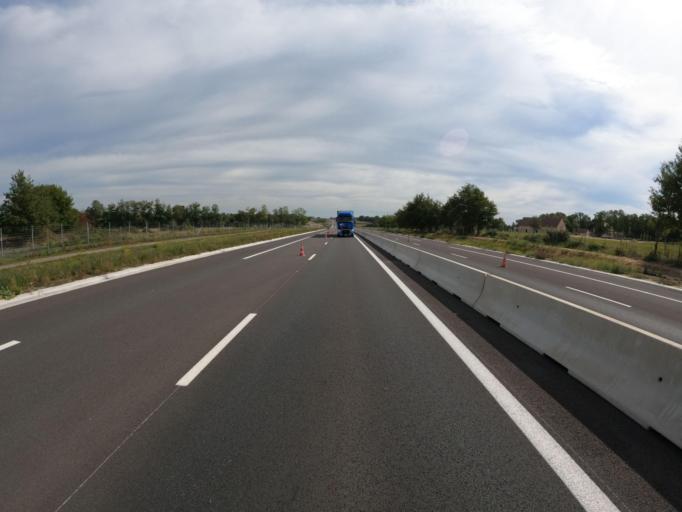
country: FR
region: Auvergne
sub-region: Departement de l'Allier
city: Lusigny
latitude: 46.5354
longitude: 3.5691
